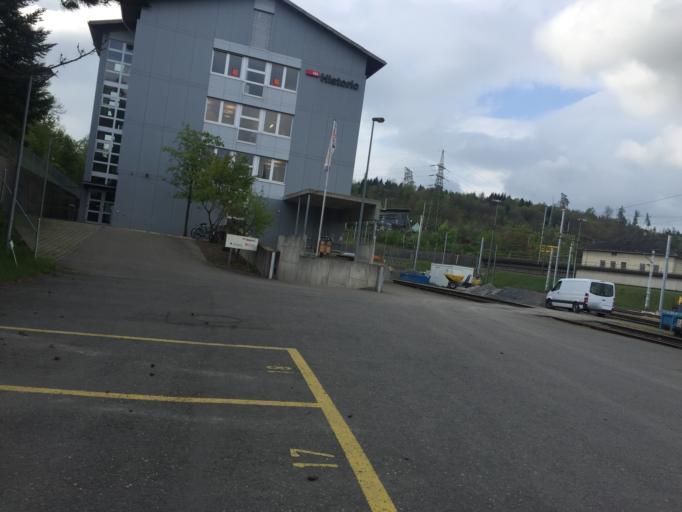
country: CH
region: Aargau
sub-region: Bezirk Brugg
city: Brugg
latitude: 47.4762
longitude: 8.2058
